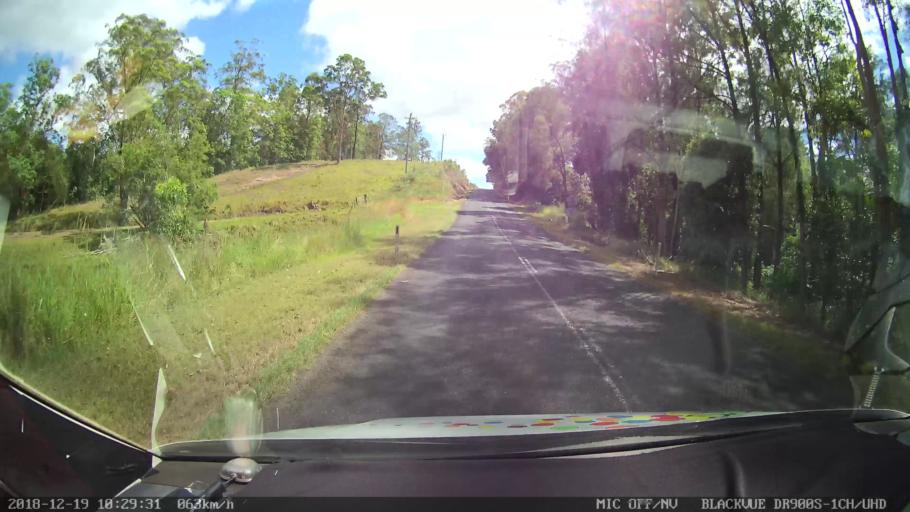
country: AU
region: New South Wales
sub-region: Lismore Municipality
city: Larnook
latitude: -28.5954
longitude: 153.1006
